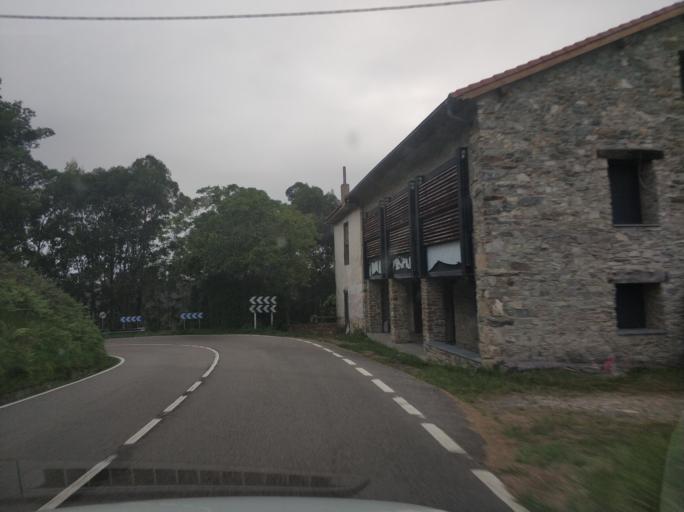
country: ES
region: Asturias
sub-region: Province of Asturias
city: Cudillero
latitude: 43.5629
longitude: -6.1803
